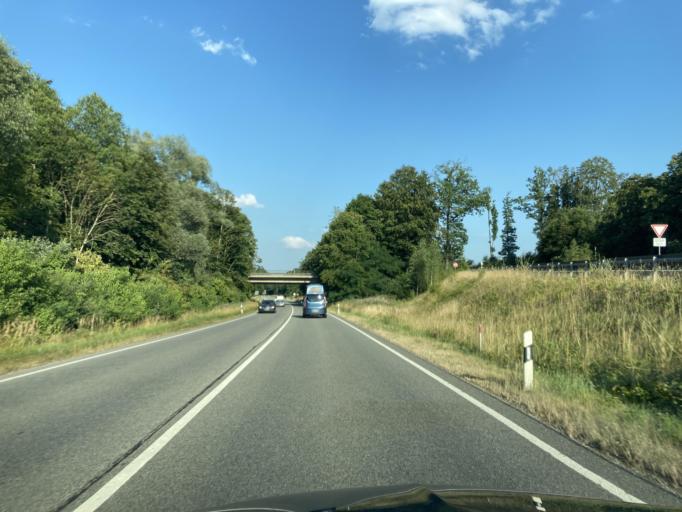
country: DE
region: Bavaria
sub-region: Upper Bavaria
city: Wasserburg am Inn
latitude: 48.0660
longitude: 12.2434
